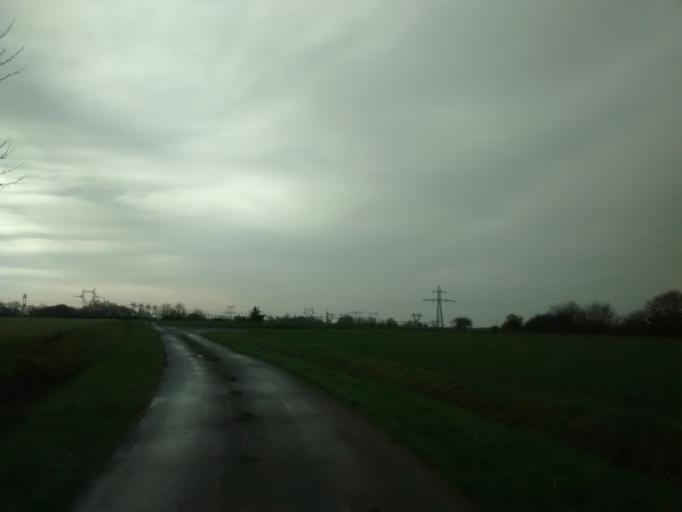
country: FR
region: Brittany
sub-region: Departement d'Ille-et-Vilaine
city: Noyal-sur-Vilaine
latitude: 48.1013
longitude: -1.5567
